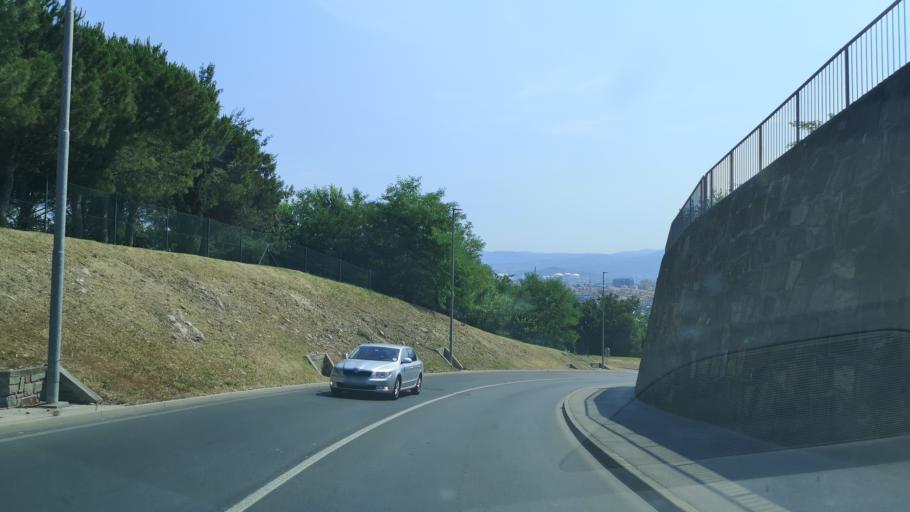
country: SI
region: Koper-Capodistria
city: Koper
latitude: 45.5435
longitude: 13.7131
